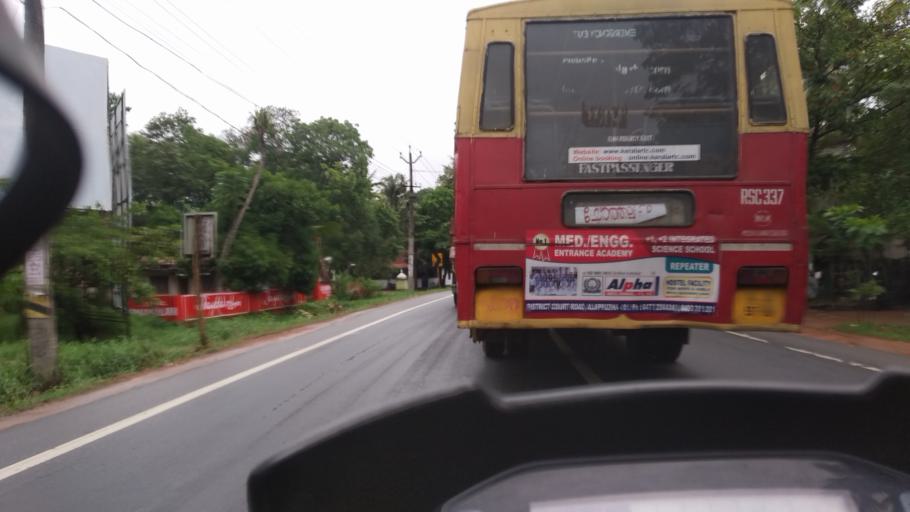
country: IN
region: Kerala
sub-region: Alappuzha
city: Mavelikara
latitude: 9.2927
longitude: 76.4348
